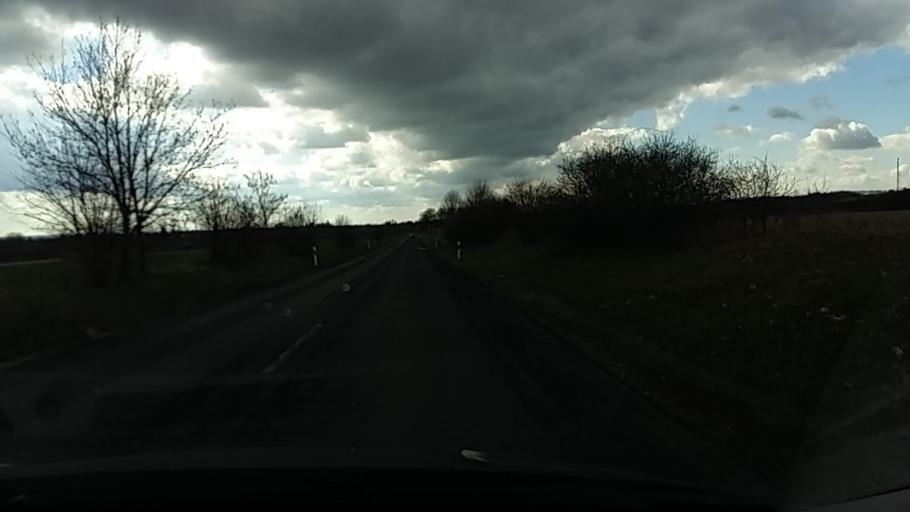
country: HU
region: Somogy
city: Bohonye
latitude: 46.4268
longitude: 17.3798
